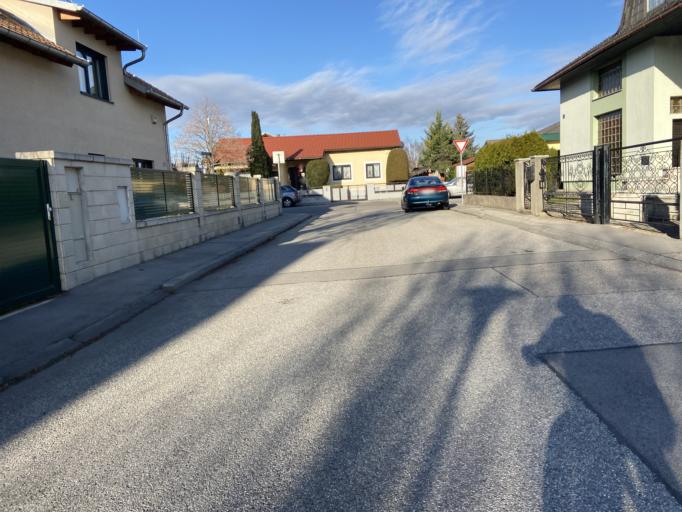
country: AT
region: Lower Austria
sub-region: Politischer Bezirk Modling
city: Guntramsdorf
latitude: 48.0543
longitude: 16.3206
